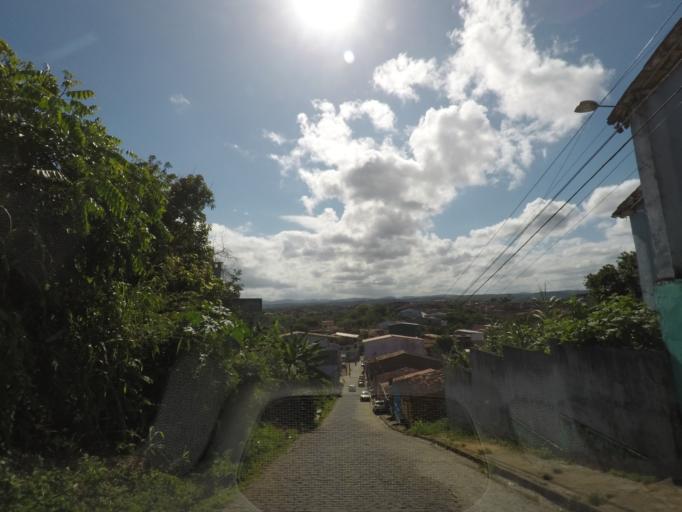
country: BR
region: Bahia
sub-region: Camamu
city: Camamu
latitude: -13.9459
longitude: -39.1054
